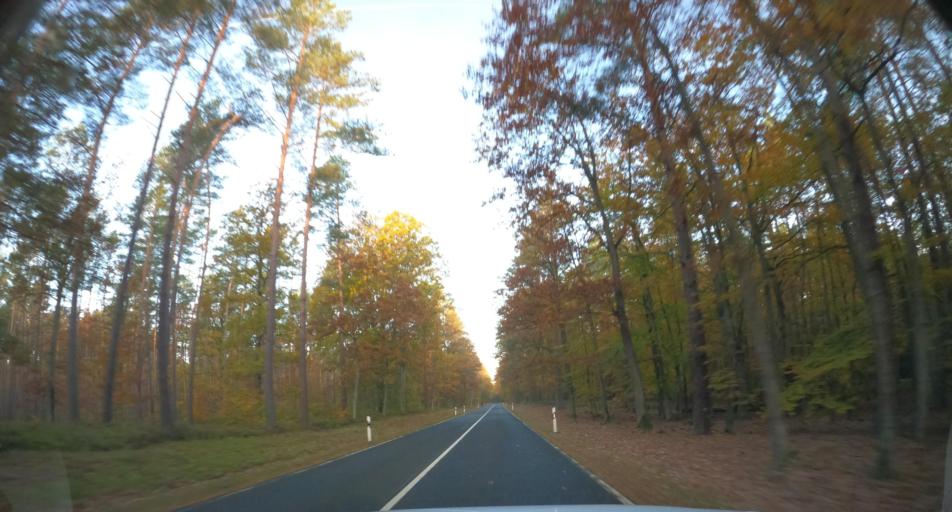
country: PL
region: West Pomeranian Voivodeship
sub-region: Powiat policki
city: Nowe Warpno
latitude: 53.6144
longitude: 14.3033
